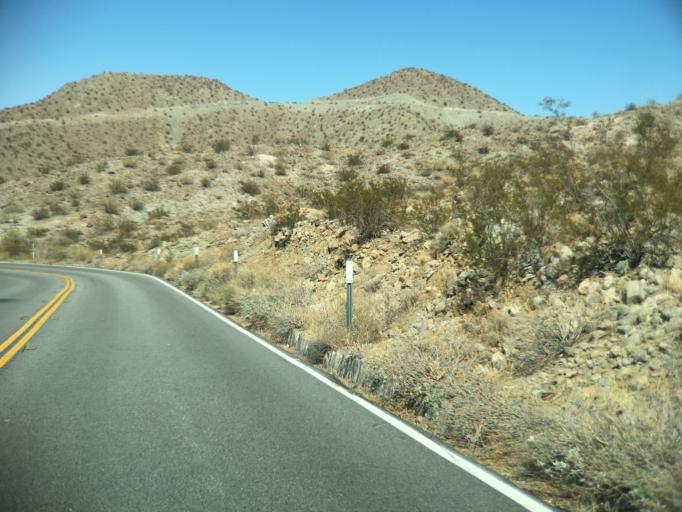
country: US
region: California
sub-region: Riverside County
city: Palm Desert
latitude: 33.6625
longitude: -116.3991
